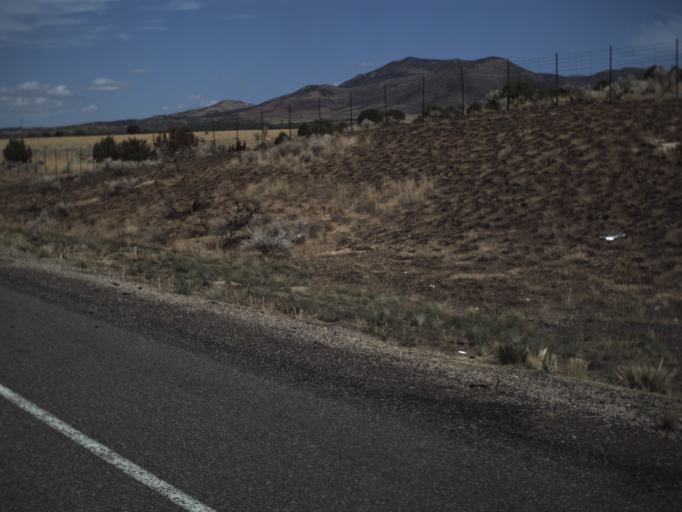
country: US
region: Utah
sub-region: Millard County
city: Fillmore
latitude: 39.1401
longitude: -112.2380
